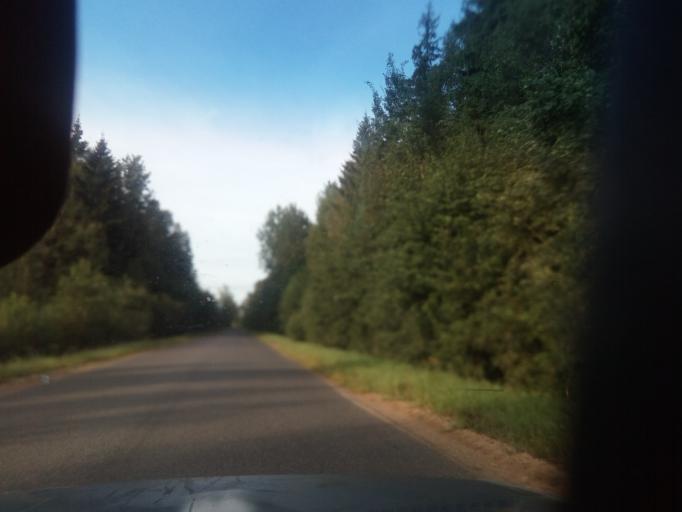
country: BY
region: Vitebsk
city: Dzisna
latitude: 55.6444
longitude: 28.3177
